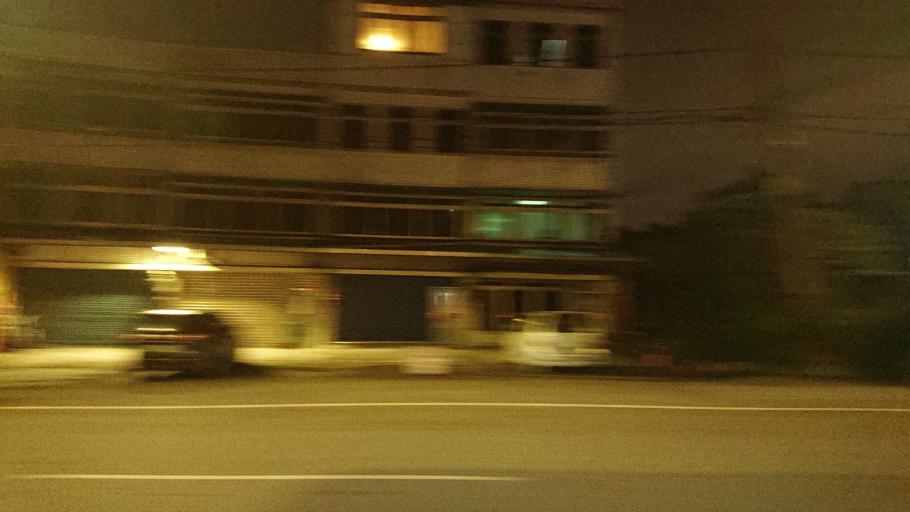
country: TW
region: Taiwan
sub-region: Taoyuan
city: Taoyuan
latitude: 24.9378
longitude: 121.3956
